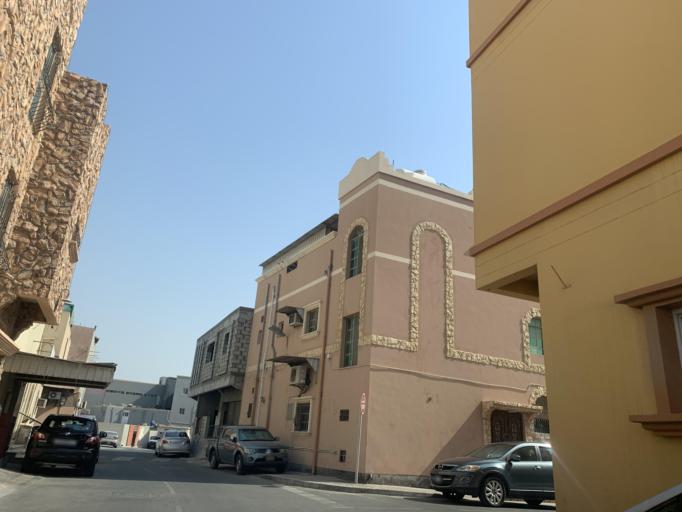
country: BH
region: Manama
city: Jidd Hafs
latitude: 26.2045
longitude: 50.5322
